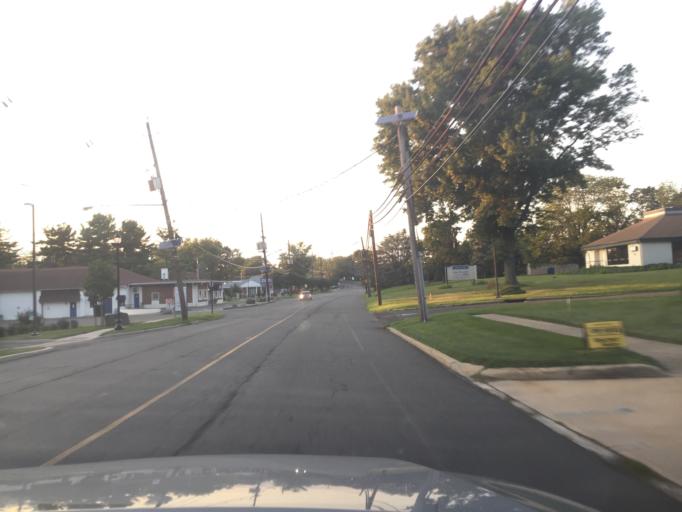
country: US
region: New Jersey
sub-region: Mercer County
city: Princeton Junction
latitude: 40.3147
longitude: -74.6199
